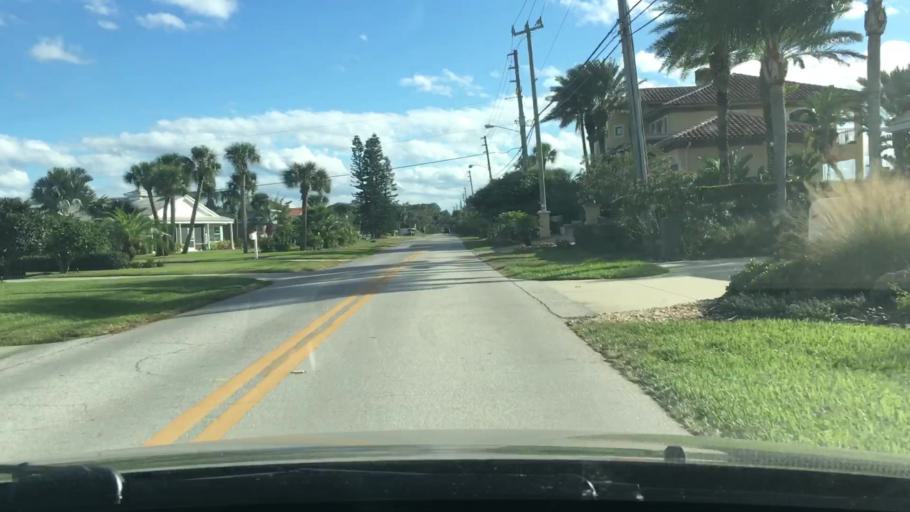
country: US
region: Florida
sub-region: Volusia County
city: Ormond-by-the-Sea
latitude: 29.3554
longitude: -81.0765
